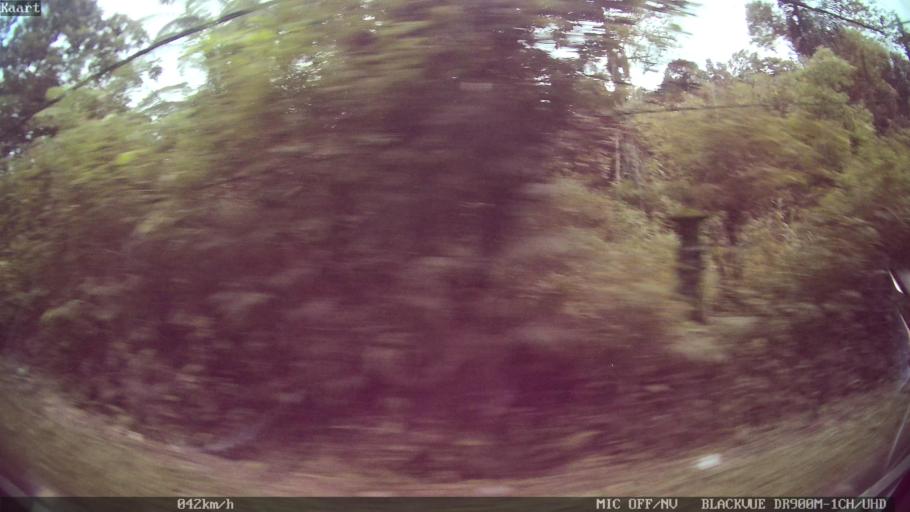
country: ID
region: Bali
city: Banjar Geriana Kangin
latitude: -8.4020
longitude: 115.4404
